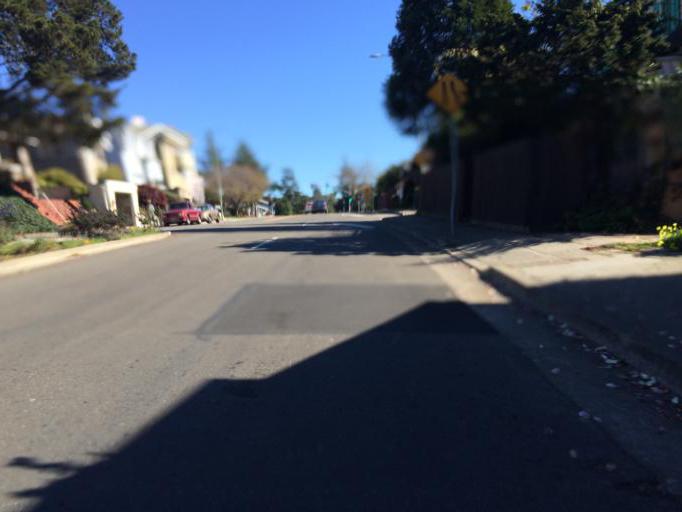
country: US
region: California
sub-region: Alameda County
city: Piedmont
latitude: 37.8287
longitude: -122.2457
